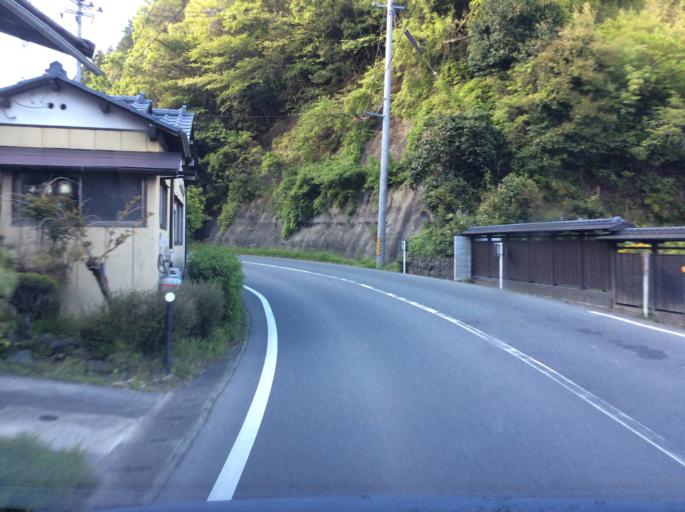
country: JP
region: Fukushima
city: Iwaki
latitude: 36.9776
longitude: 140.8438
